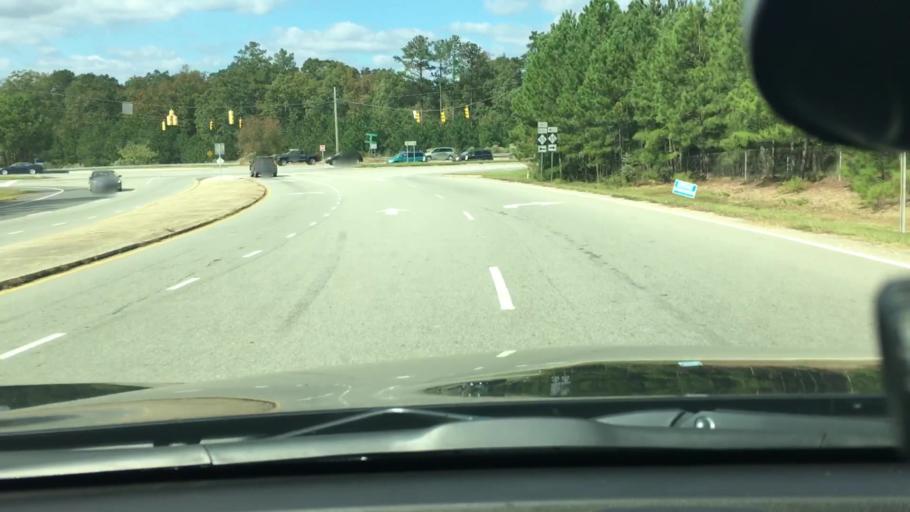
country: US
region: North Carolina
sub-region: Wake County
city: Apex
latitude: 35.6941
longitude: -78.8343
